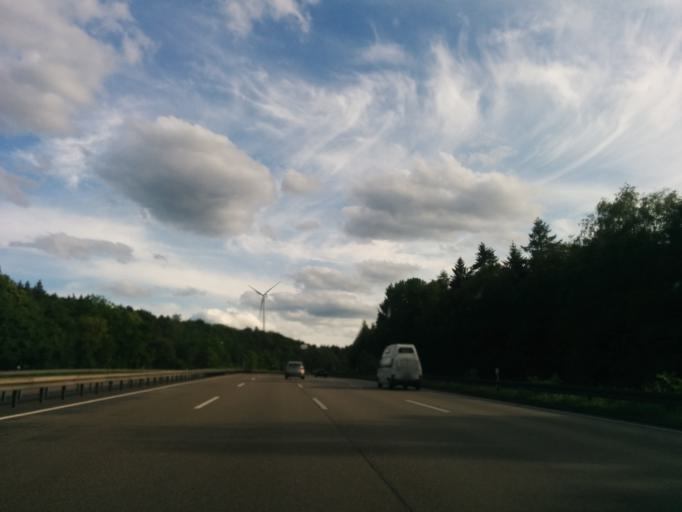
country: DE
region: Hesse
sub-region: Regierungsbezirk Kassel
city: Lohfelden
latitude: 51.2533
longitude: 9.5170
